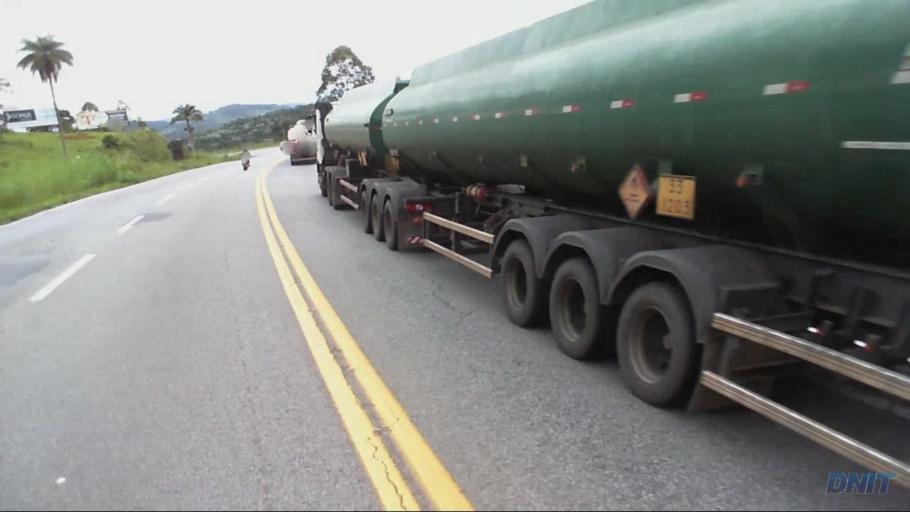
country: BR
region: Minas Gerais
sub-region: Caete
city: Caete
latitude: -19.7403
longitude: -43.5173
